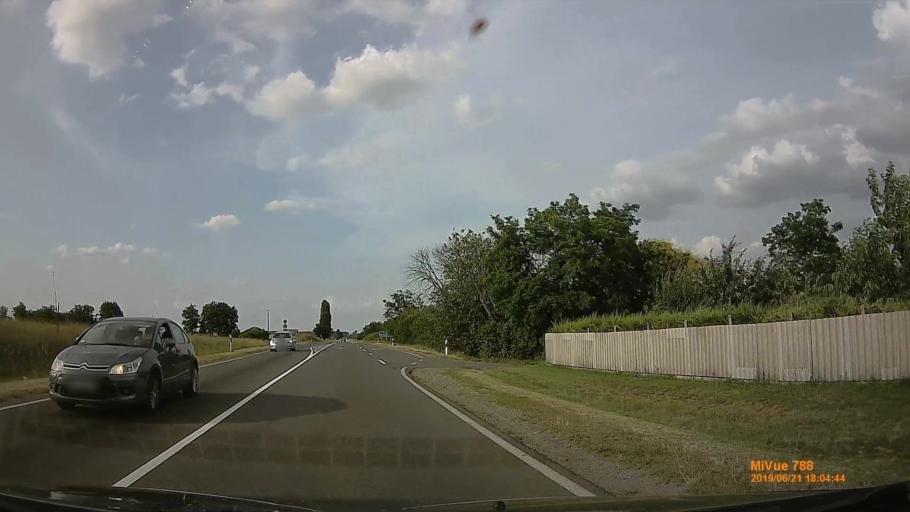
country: HU
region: Tolna
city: Dunaszentgyorgy
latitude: 46.5336
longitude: 18.8096
